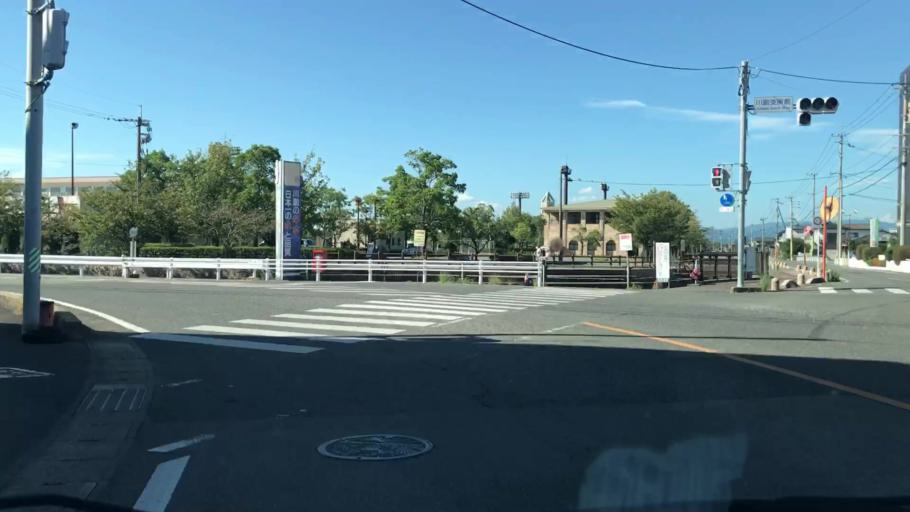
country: JP
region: Saga Prefecture
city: Okawa
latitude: 33.1913
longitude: 130.3195
